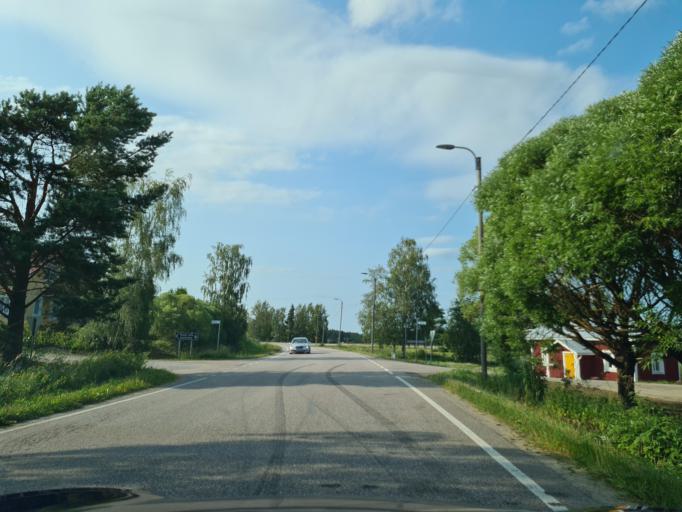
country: FI
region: Ostrobothnia
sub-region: Vaasa
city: Vaehaekyroe
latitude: 63.0096
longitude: 22.1491
